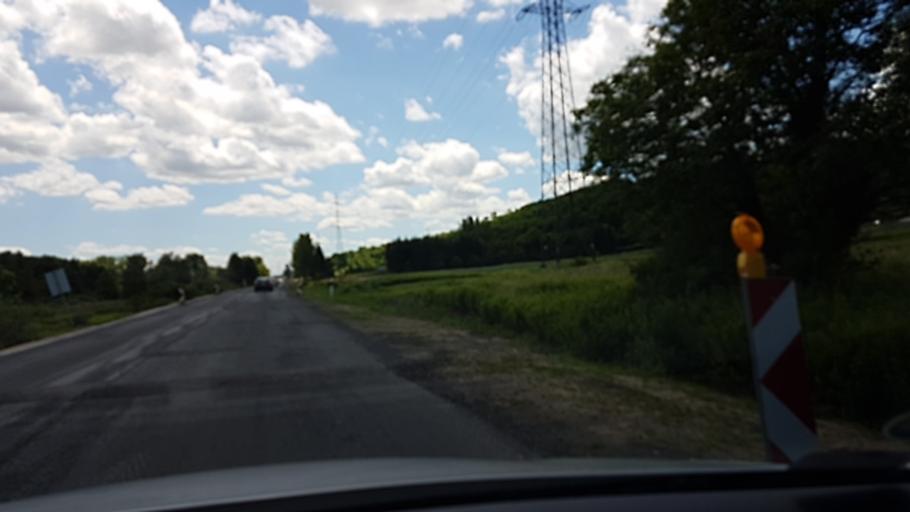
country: HU
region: Zala
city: Zalaegerszeg
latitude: 46.8271
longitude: 16.8634
